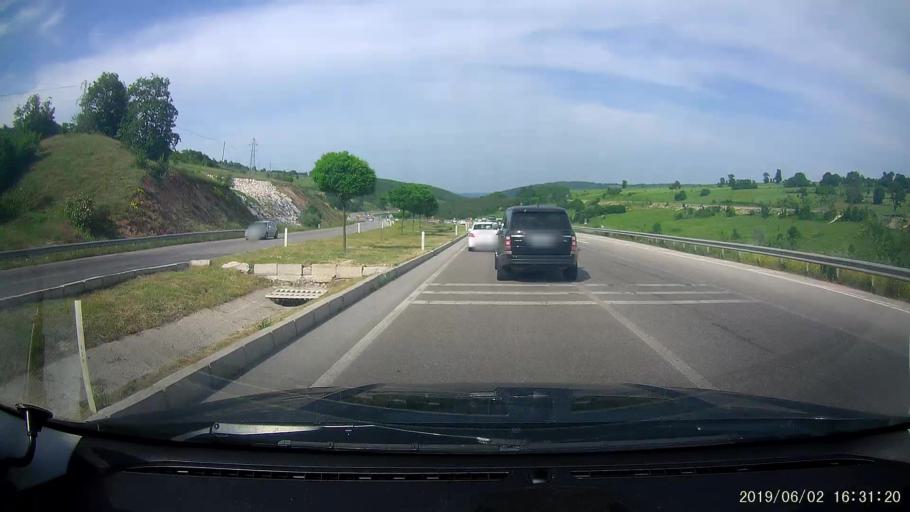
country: TR
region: Samsun
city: Ladik
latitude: 41.0313
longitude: 35.8997
